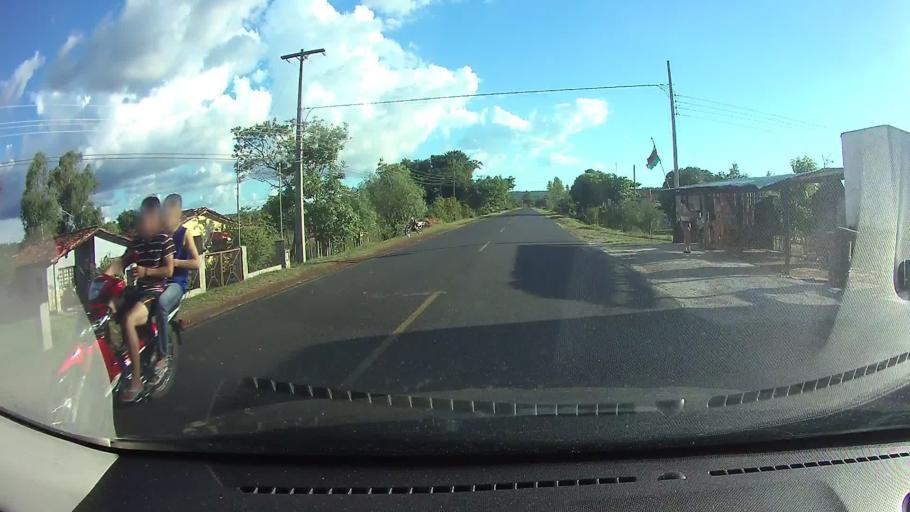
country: PY
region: Cordillera
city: Emboscada
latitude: -25.1533
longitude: -57.2613
